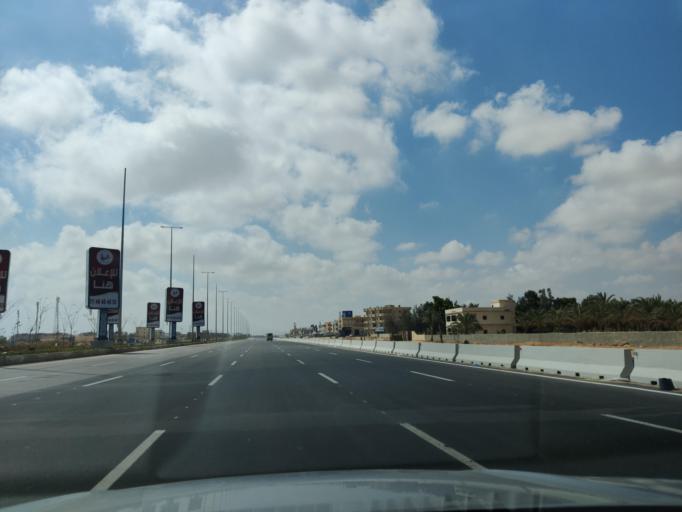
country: EG
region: Muhafazat Matruh
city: Al `Alamayn
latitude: 30.9459
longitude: 28.7771
